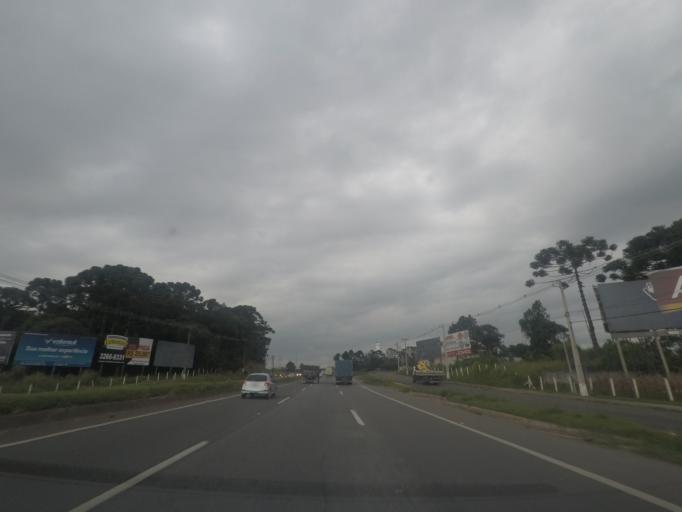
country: BR
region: Parana
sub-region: Sao Jose Dos Pinhais
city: Sao Jose dos Pinhais
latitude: -25.5738
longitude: -49.1801
